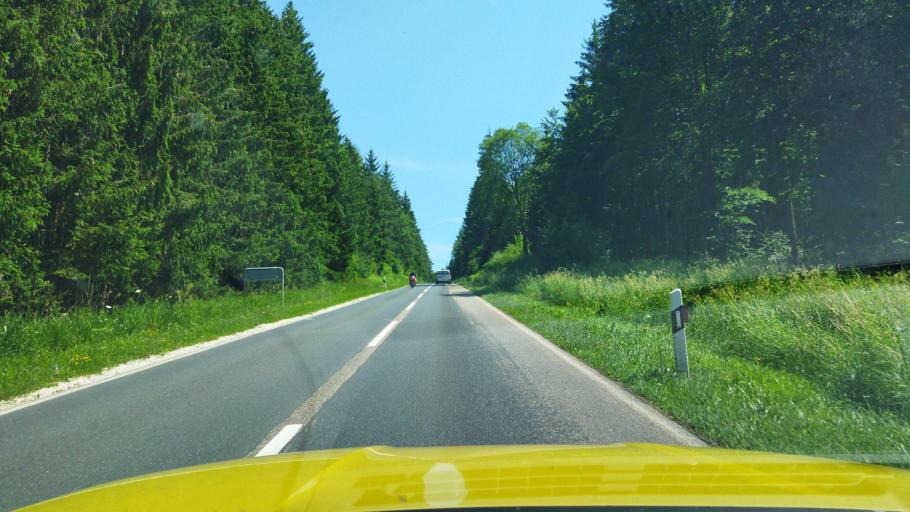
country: DE
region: Bavaria
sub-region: Lower Bavaria
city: Riedenburg
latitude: 48.9494
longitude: 11.6487
